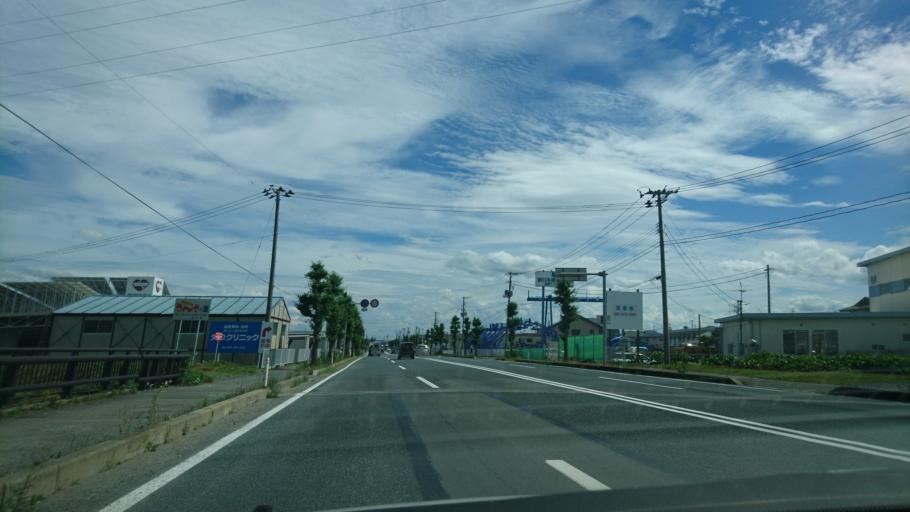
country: JP
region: Iwate
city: Morioka-shi
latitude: 39.6318
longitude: 141.1736
